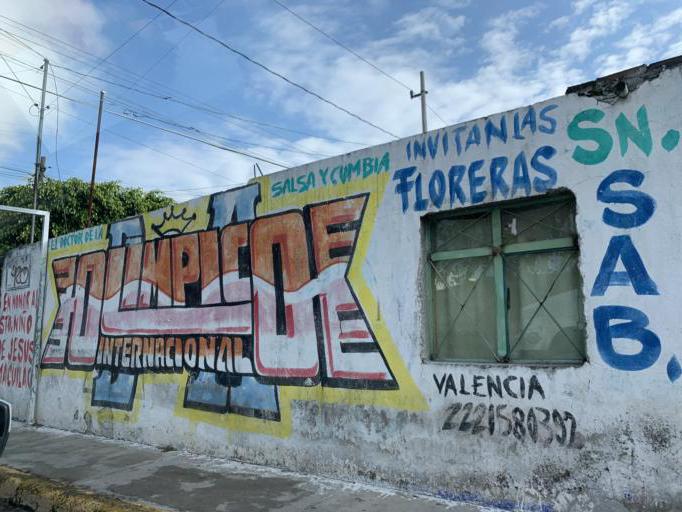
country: MX
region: Puebla
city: San Andres Cholula
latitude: 19.0539
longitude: -98.2941
